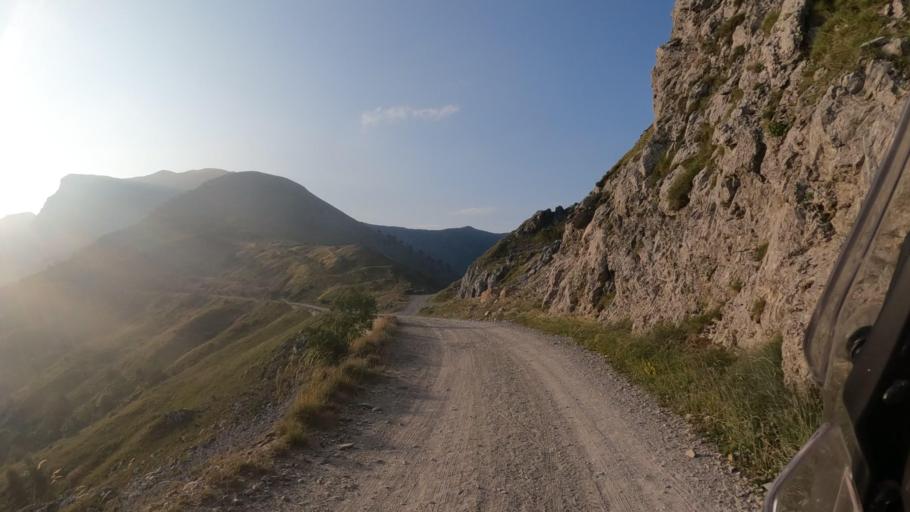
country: IT
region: Piedmont
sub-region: Provincia di Cuneo
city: Limone Piemonte
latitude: 44.1530
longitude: 7.5772
